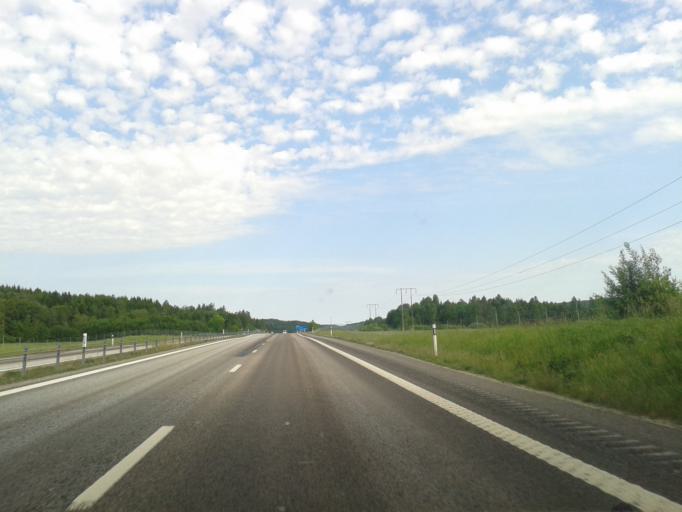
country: SE
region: Vaestra Goetaland
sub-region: Munkedals Kommun
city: Munkedal
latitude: 58.5068
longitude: 11.5609
